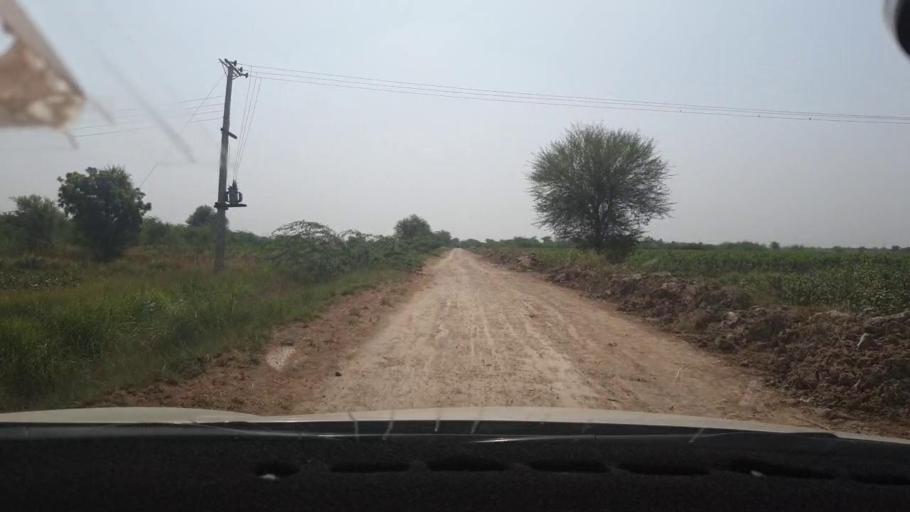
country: PK
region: Sindh
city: Tando Mittha Khan
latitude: 25.9308
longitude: 69.2247
